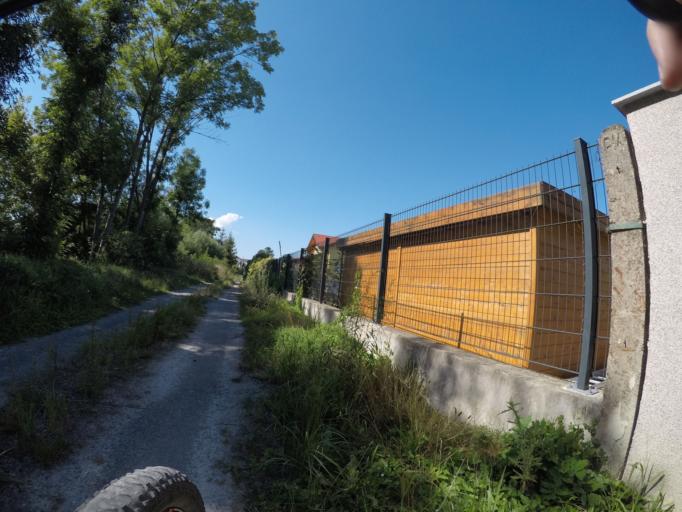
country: AT
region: Lower Austria
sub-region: Politischer Bezirk Wien-Umgebung
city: Moosbrunn
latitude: 48.0101
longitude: 16.4551
